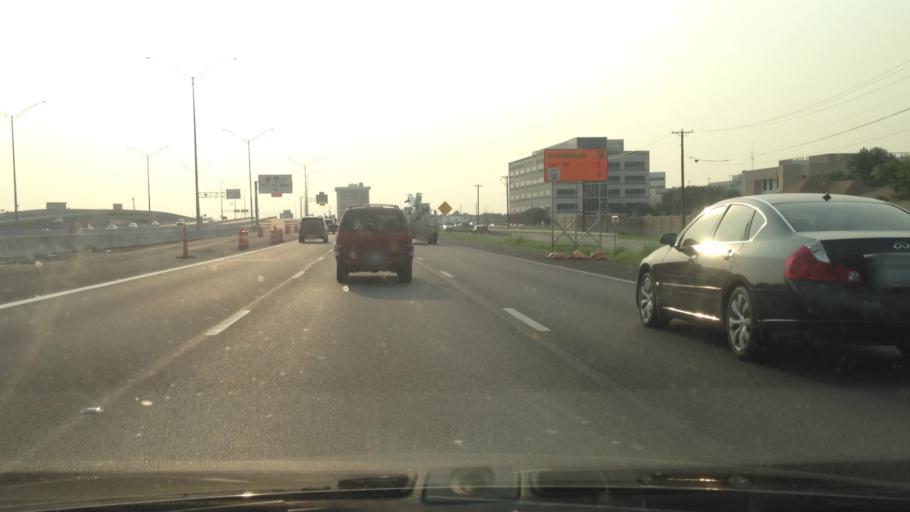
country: US
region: Texas
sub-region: Dallas County
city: Irving
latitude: 32.8365
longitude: -96.9657
